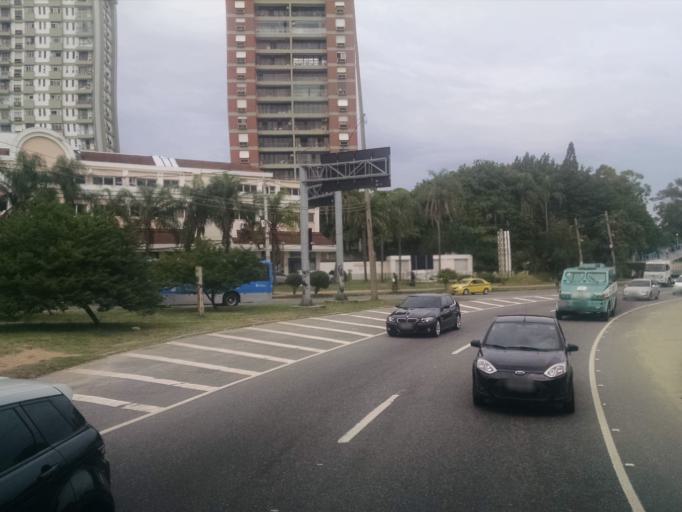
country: BR
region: Rio de Janeiro
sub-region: Rio De Janeiro
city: Rio de Janeiro
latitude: -23.0002
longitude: -43.3630
